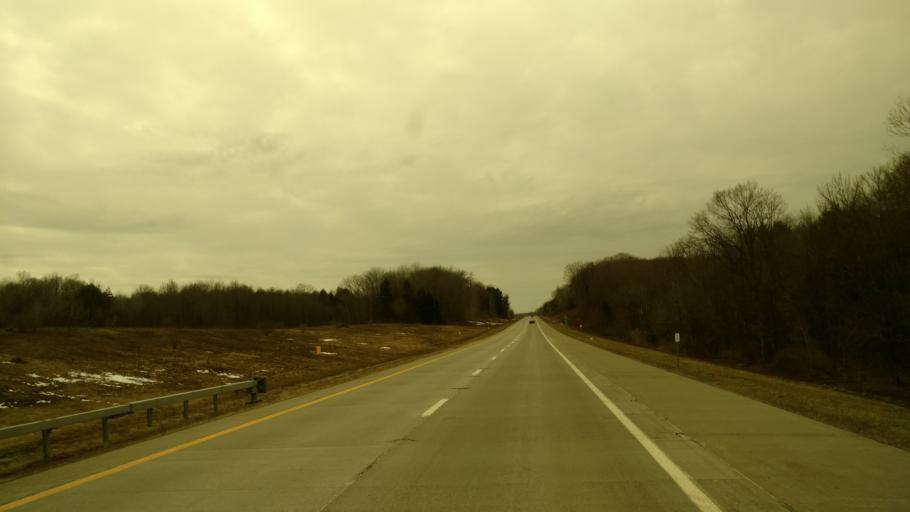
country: US
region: New York
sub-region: Chautauqua County
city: Mayville
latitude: 42.1551
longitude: -79.4528
